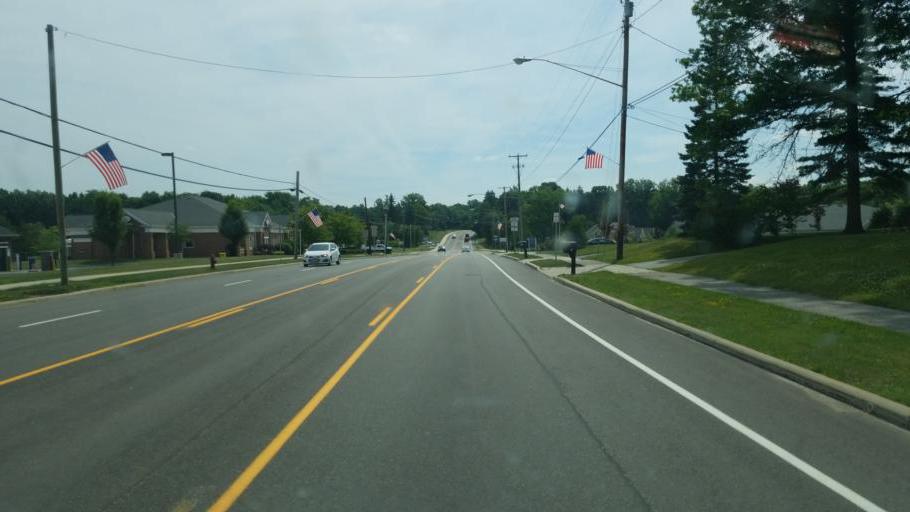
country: US
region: Ohio
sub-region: Summit County
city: Macedonia
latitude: 41.3137
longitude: -81.5022
